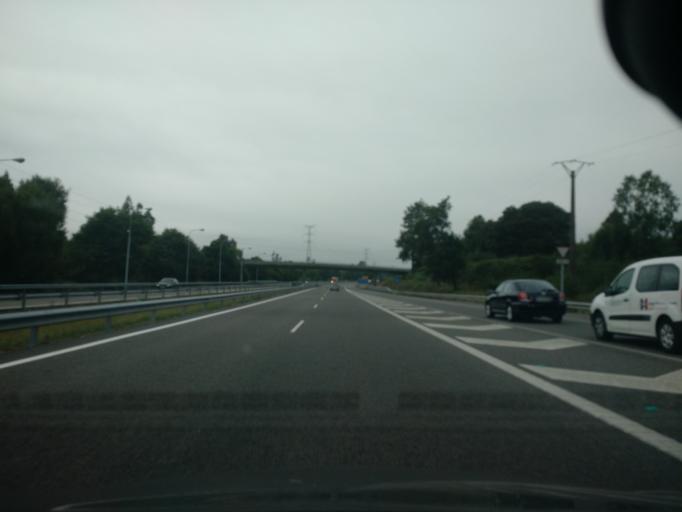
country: ES
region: Galicia
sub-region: Provincia da Coruna
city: Ordes
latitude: 43.0958
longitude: -8.3510
